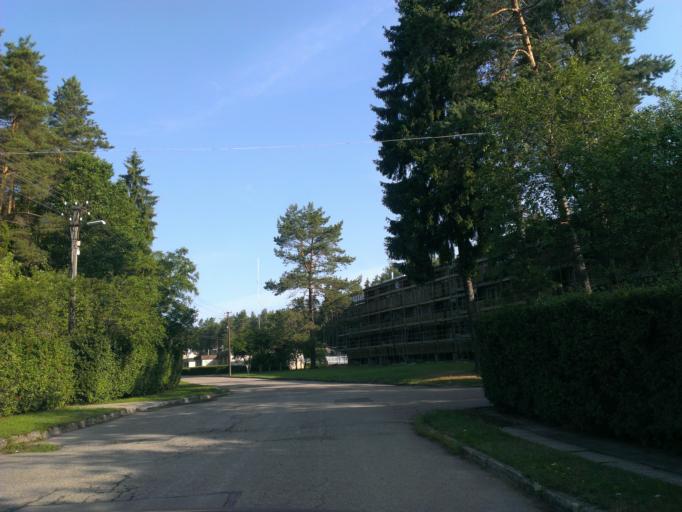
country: LV
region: Incukalns
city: Vangazi
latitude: 57.0944
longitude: 24.5512
